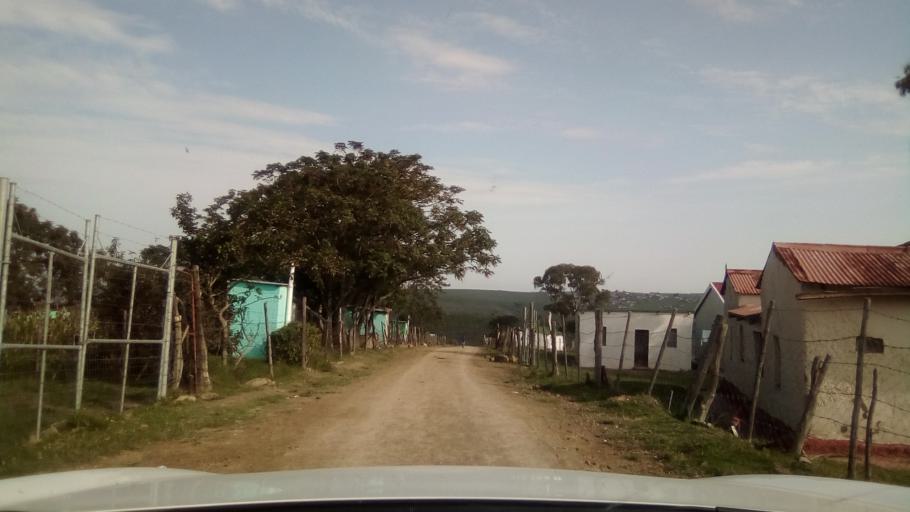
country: ZA
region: Eastern Cape
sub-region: Buffalo City Metropolitan Municipality
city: Bhisho
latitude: -33.0063
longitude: 27.3007
